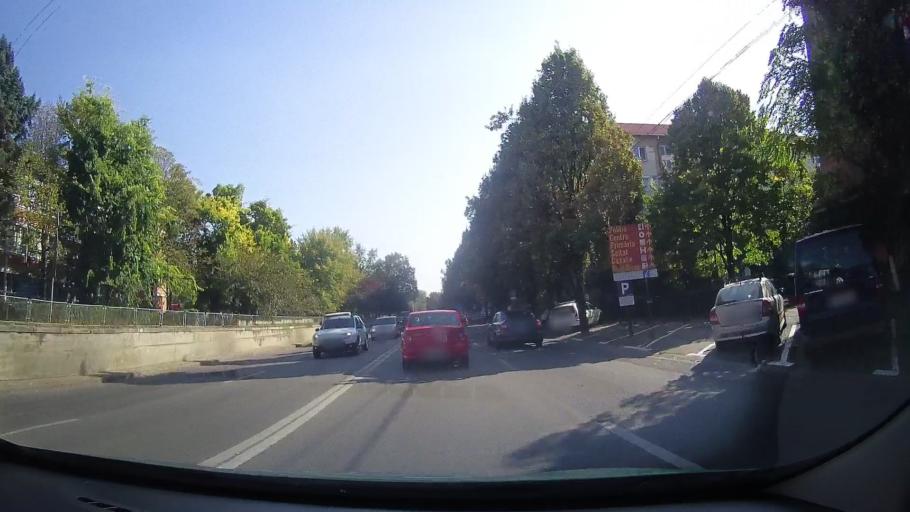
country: RO
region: Bihor
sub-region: Comuna Biharea
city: Oradea
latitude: 47.0682
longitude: 21.9277
